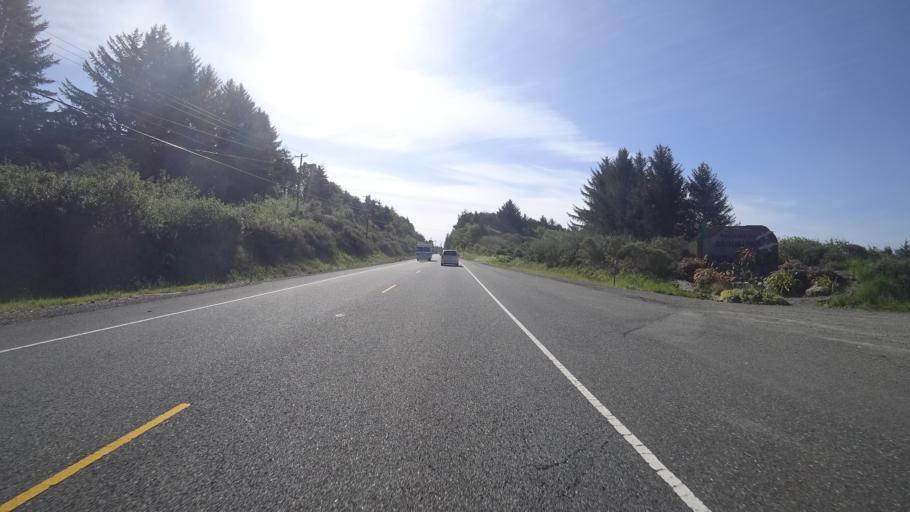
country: US
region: Oregon
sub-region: Curry County
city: Brookings
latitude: 42.0832
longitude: -124.3233
